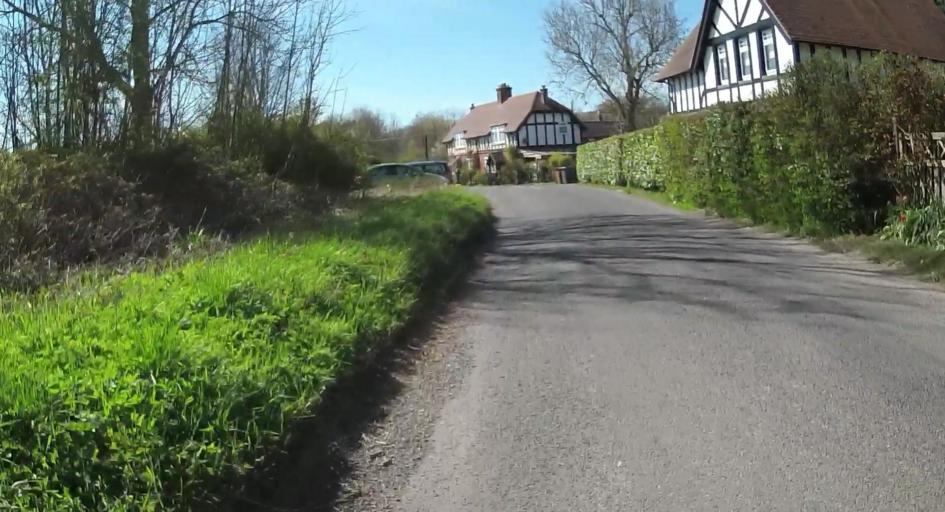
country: GB
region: England
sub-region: Hampshire
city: Romsey
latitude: 51.0718
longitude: -1.5067
